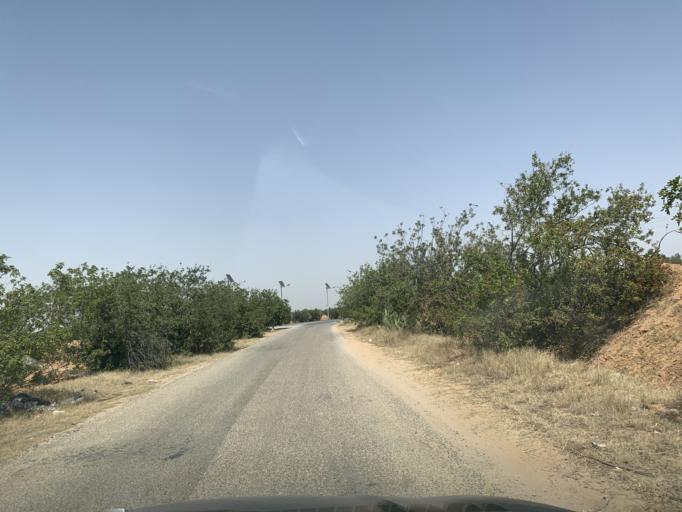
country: TN
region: Al Mahdiyah
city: Shurban
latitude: 35.1940
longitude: 10.2523
